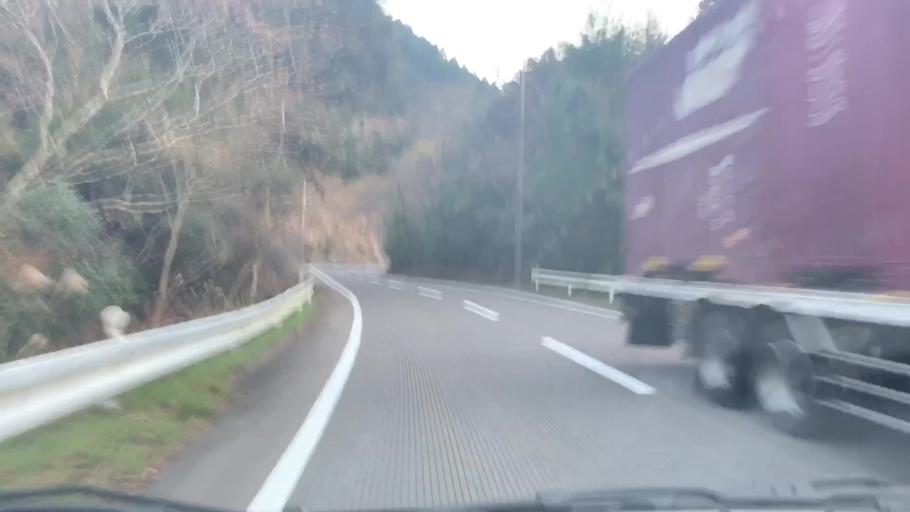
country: JP
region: Saga Prefecture
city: Kashima
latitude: 33.0019
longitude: 130.0632
